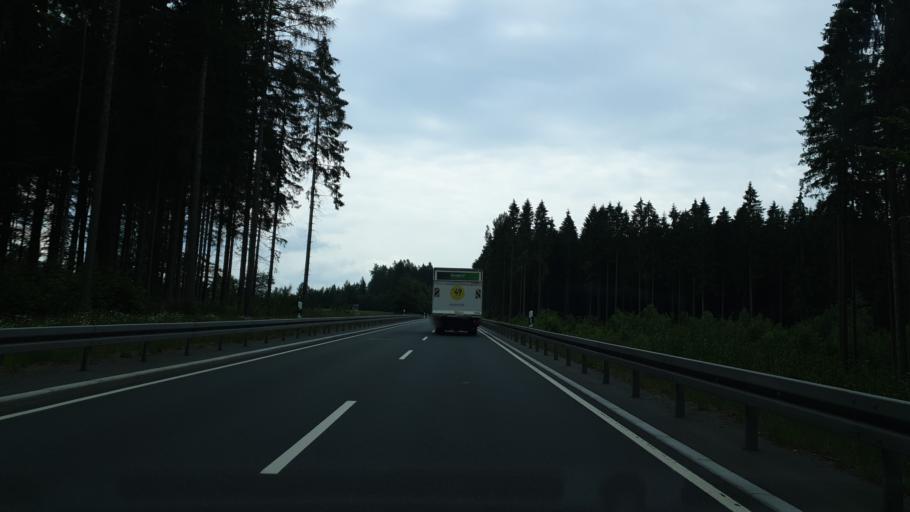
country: DE
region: Saxony
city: Tannenbergsthal
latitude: 50.4639
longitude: 12.4400
